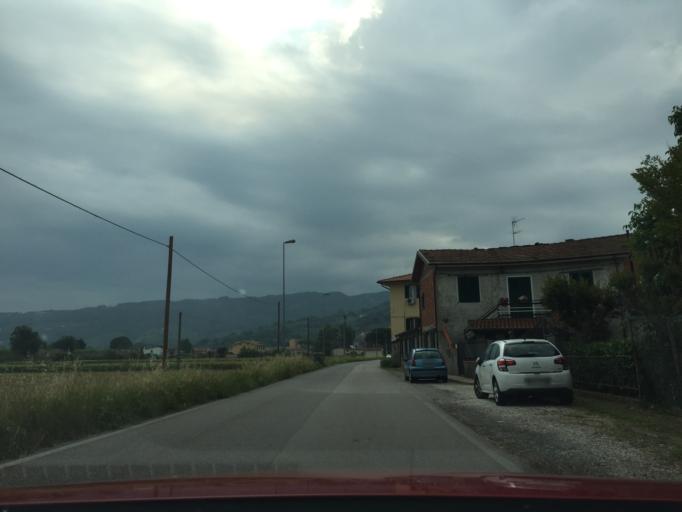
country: IT
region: Tuscany
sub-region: Provincia di Pistoia
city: Pieve a Nievole
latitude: 43.8772
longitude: 10.8014
